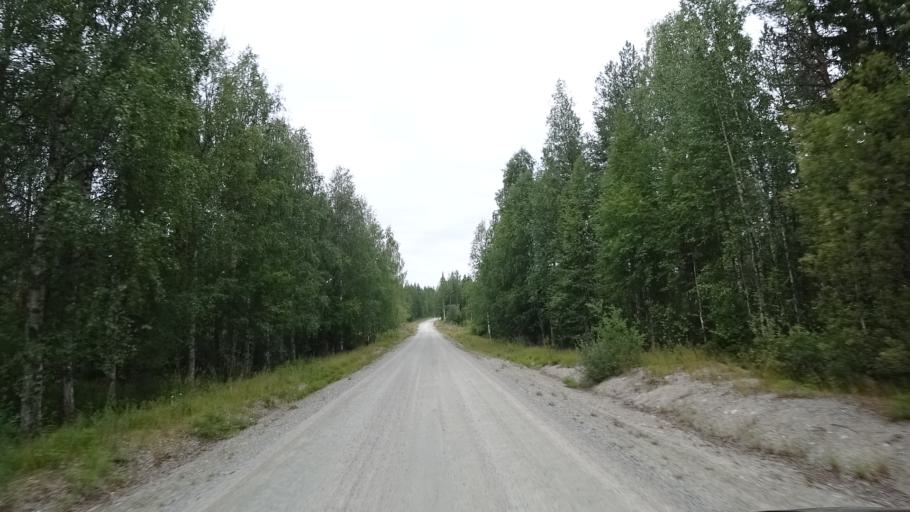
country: FI
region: North Karelia
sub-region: Joensuu
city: Ilomantsi
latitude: 63.1540
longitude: 30.6192
